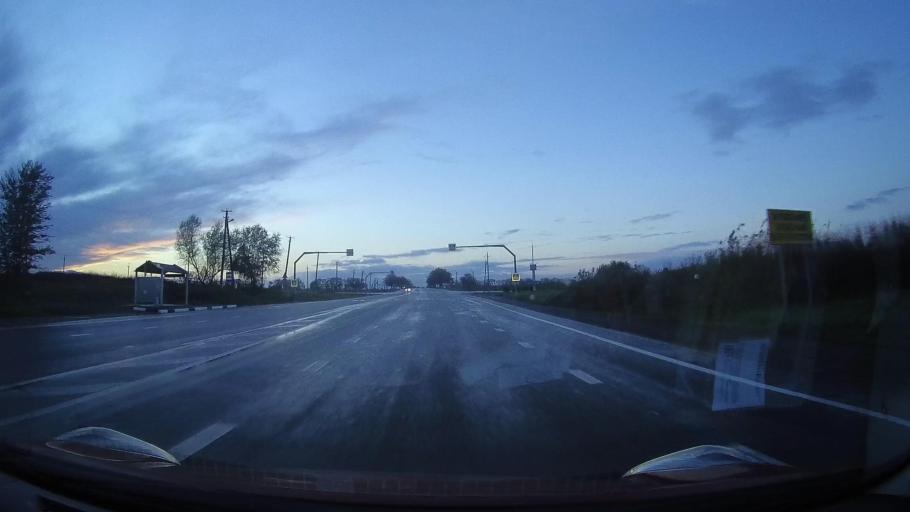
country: RU
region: Krasnodarskiy
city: Konokovo
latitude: 44.8293
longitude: 41.3422
